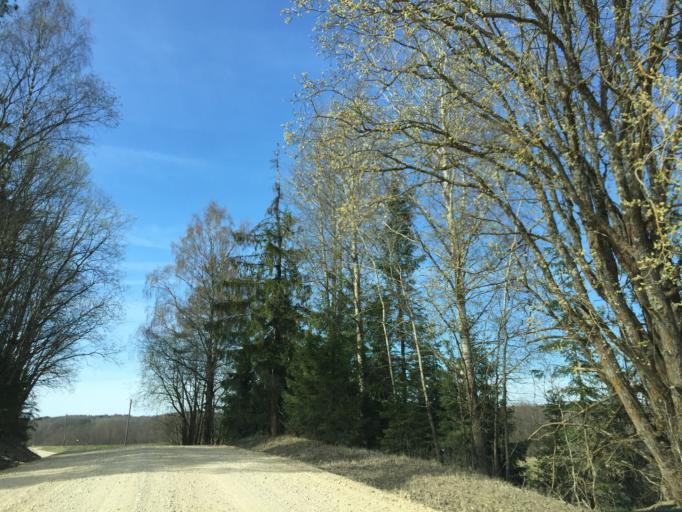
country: EE
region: Vorumaa
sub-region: Antsla vald
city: Vana-Antsla
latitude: 57.9536
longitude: 26.3647
